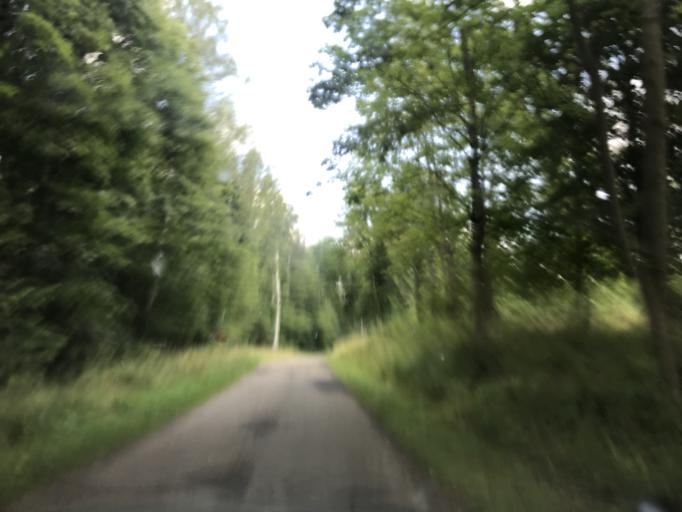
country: PL
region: West Pomeranian Voivodeship
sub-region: Powiat lobeski
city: Wegorzyno
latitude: 53.5035
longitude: 15.4926
